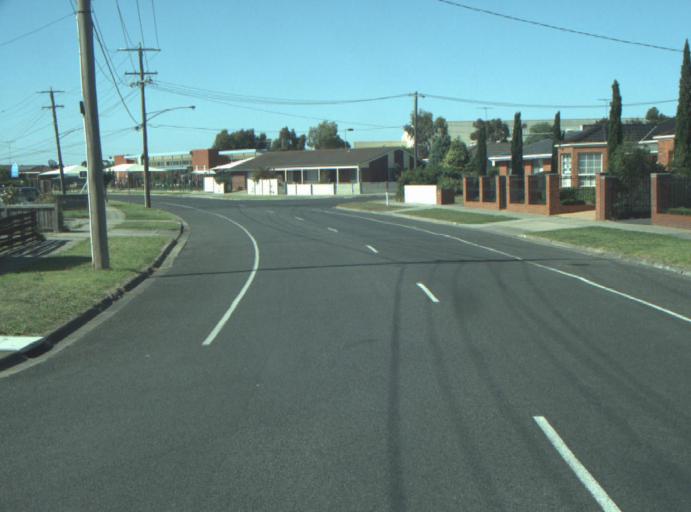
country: AU
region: Victoria
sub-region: Greater Geelong
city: Bell Post Hill
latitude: -38.0878
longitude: 144.3380
